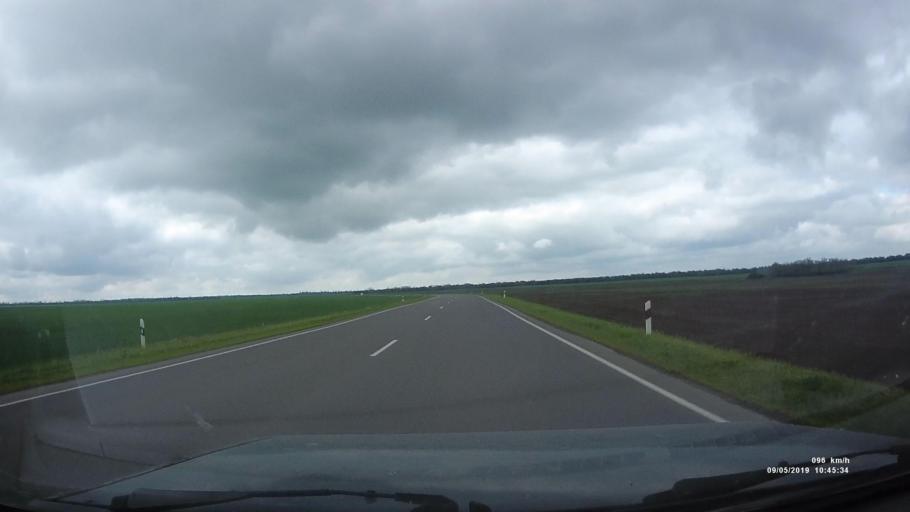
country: RU
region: Rostov
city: Peshkovo
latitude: 46.9940
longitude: 39.3648
